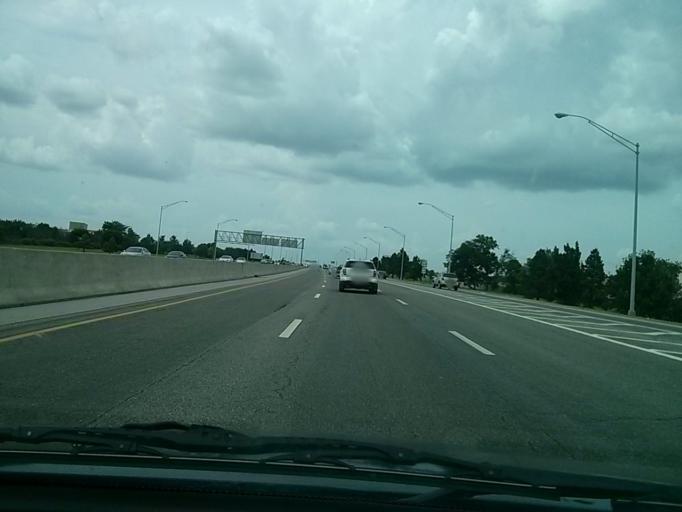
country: US
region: Oklahoma
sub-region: Tulsa County
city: Broken Arrow
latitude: 36.0377
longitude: -95.8589
